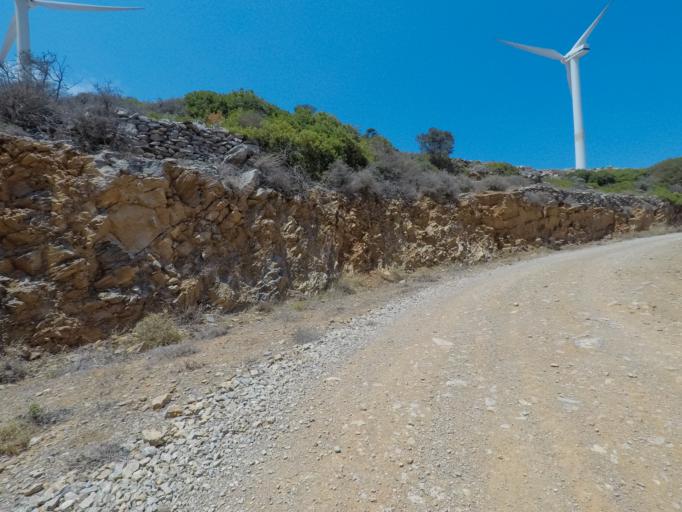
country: GR
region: Crete
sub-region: Nomos Lasithiou
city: Elounda
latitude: 35.3281
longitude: 25.7576
